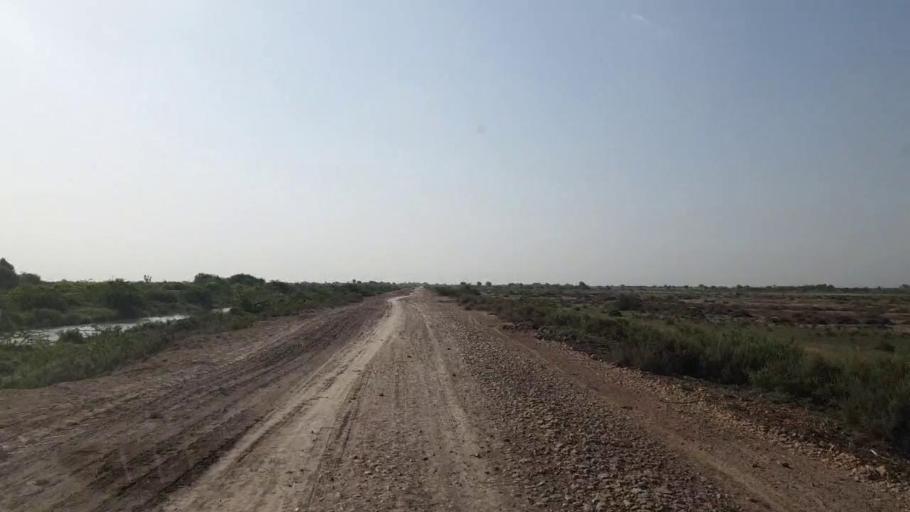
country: PK
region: Sindh
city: Kadhan
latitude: 24.6339
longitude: 69.0726
